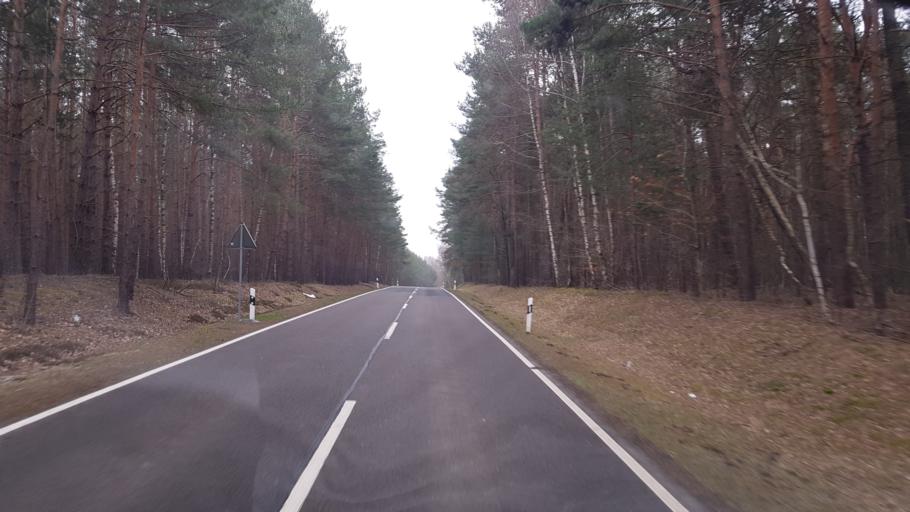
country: DE
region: Brandenburg
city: Crinitz
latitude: 51.7406
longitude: 13.8400
